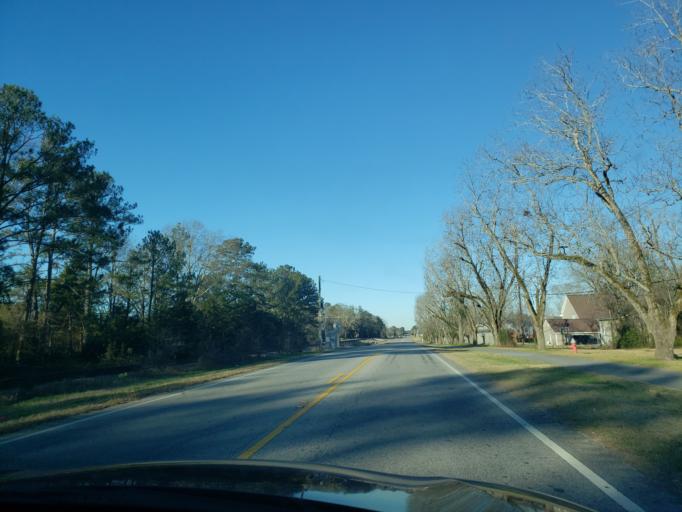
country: US
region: Alabama
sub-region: Lee County
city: Auburn
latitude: 32.6019
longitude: -85.5306
